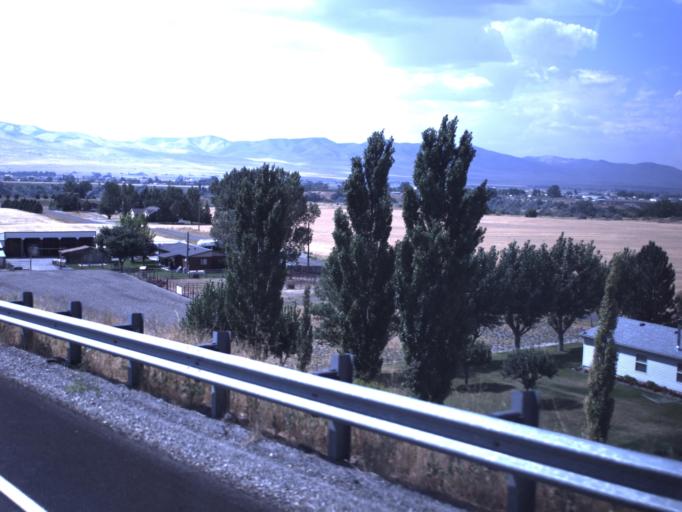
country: US
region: Utah
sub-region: Box Elder County
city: Garland
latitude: 41.7849
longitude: -112.0938
